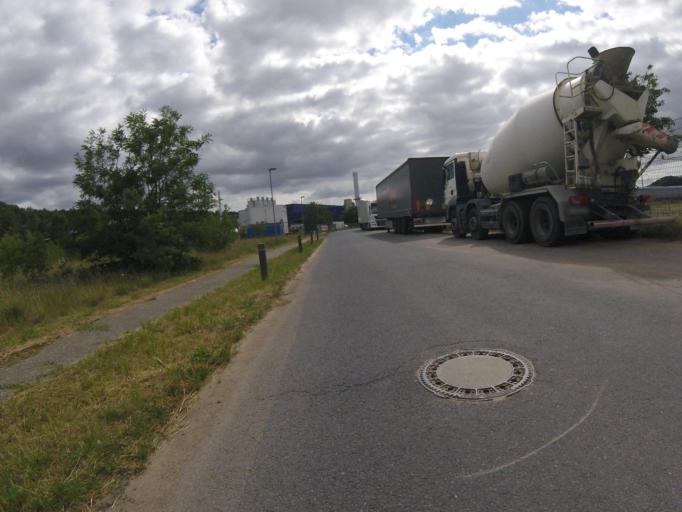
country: DE
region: Brandenburg
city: Wildau
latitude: 52.3199
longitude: 13.6766
